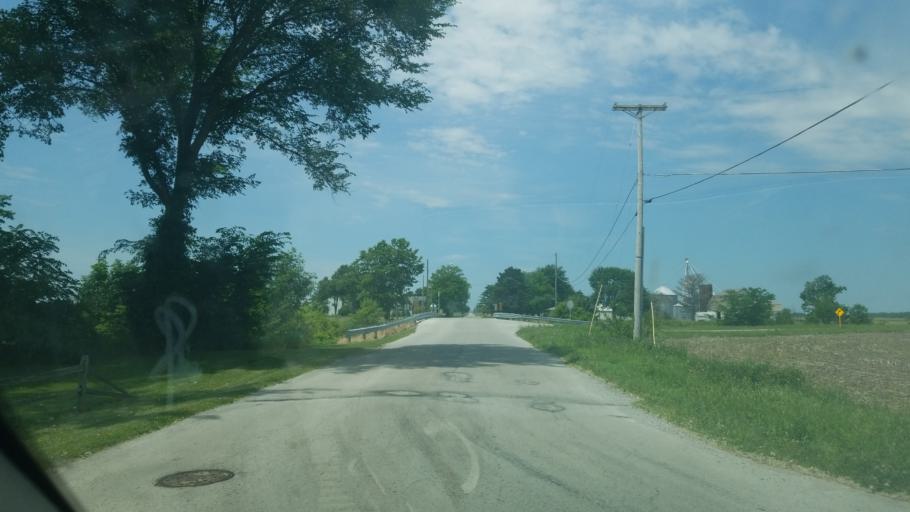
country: US
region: Ohio
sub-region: Wood County
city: North Baltimore
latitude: 41.2538
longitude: -83.6101
